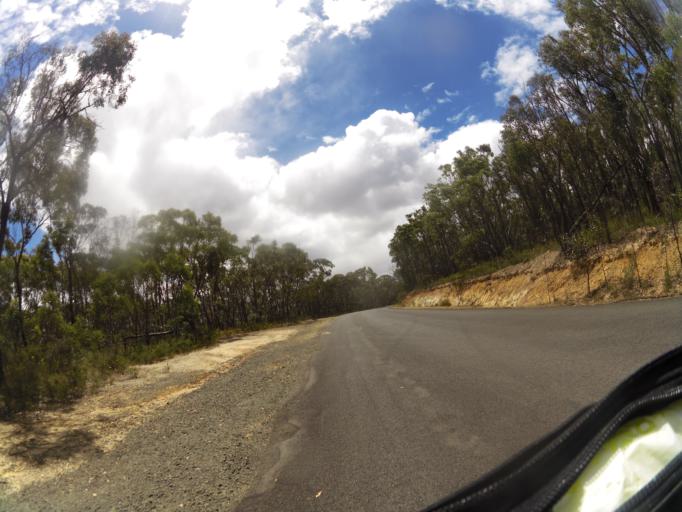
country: AU
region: Victoria
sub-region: Mount Alexander
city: Castlemaine
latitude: -37.0223
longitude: 144.2427
